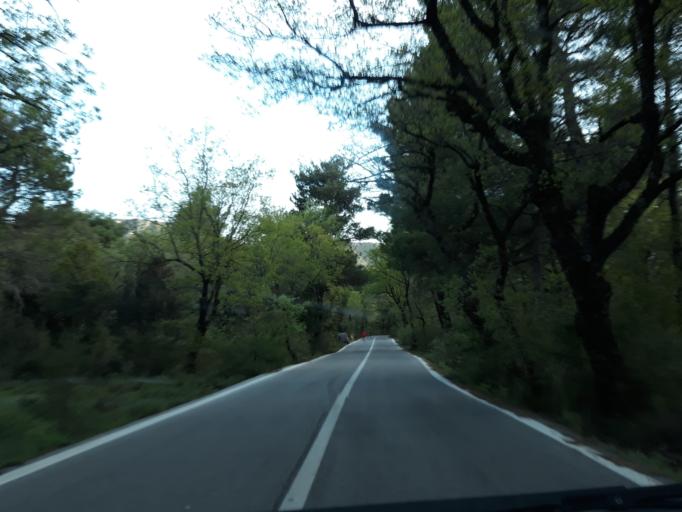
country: GR
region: Attica
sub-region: Nomarchia Anatolikis Attikis
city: Afidnes
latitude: 38.2010
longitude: 23.7868
